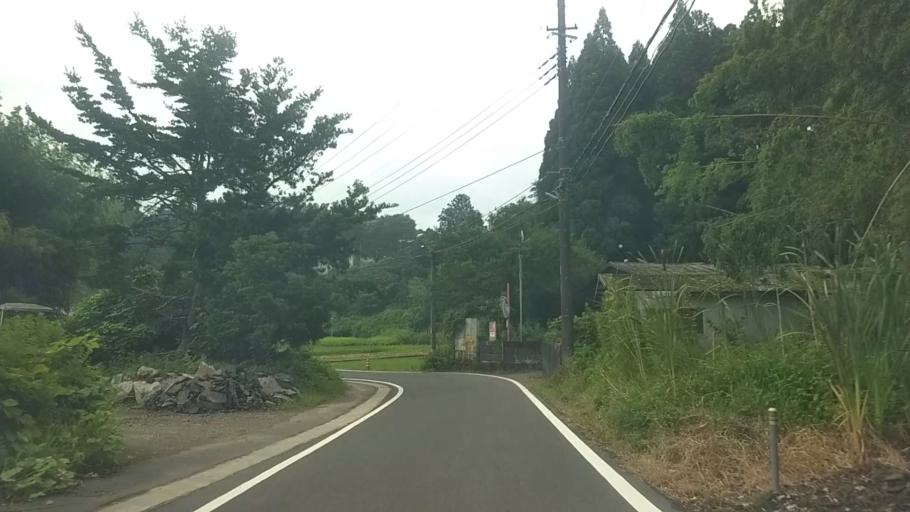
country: JP
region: Chiba
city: Kawaguchi
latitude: 35.2548
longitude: 140.0579
